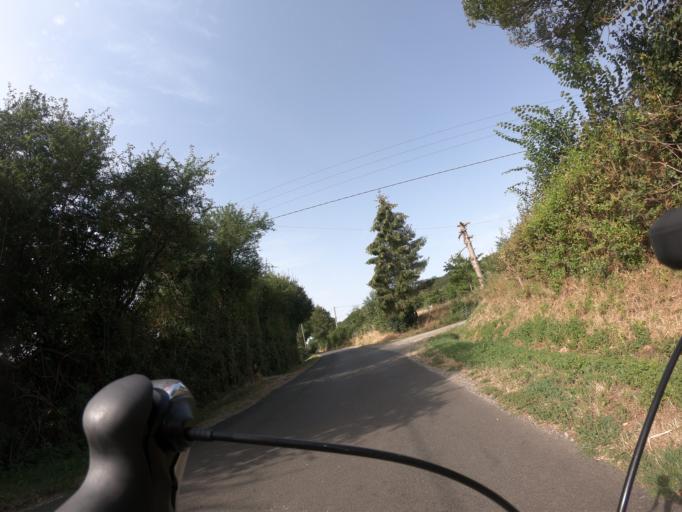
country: FR
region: Lower Normandy
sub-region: Departement de l'Orne
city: Conde-sur-Huisne
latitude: 48.3634
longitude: 0.8390
